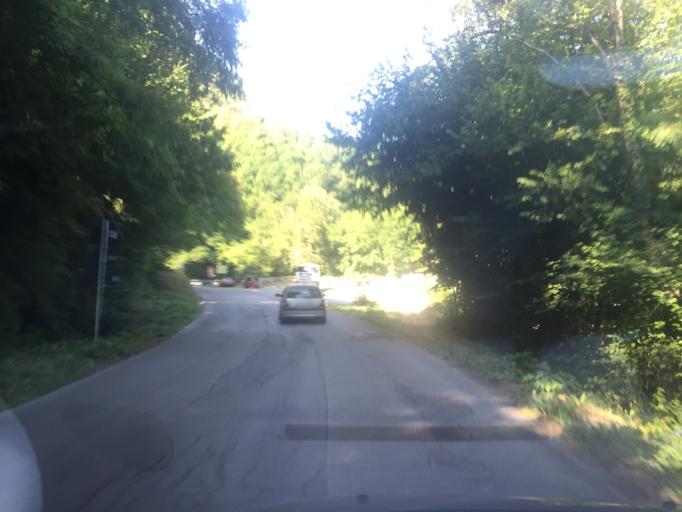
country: IT
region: Tuscany
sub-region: Provincia di Lucca
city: Careggine
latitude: 44.1370
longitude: 10.3299
